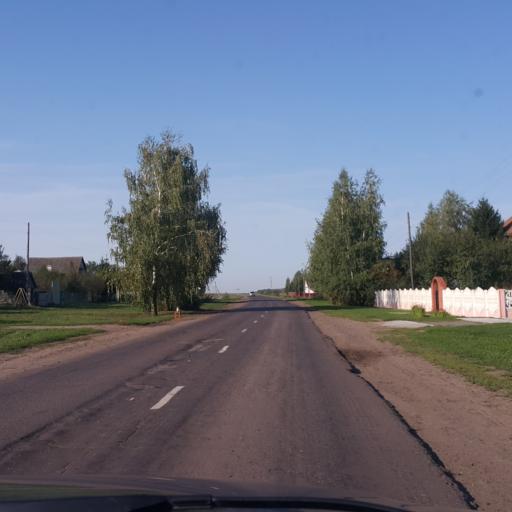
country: RU
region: Tambov
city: Novaya Lyada
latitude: 52.7712
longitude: 41.7468
